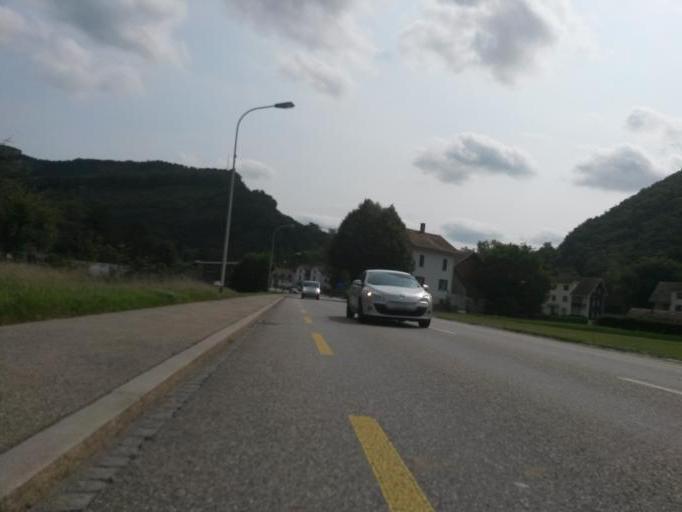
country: CH
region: Solothurn
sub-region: Bezirk Thal
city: Balsthal
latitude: 47.3107
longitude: 7.6857
